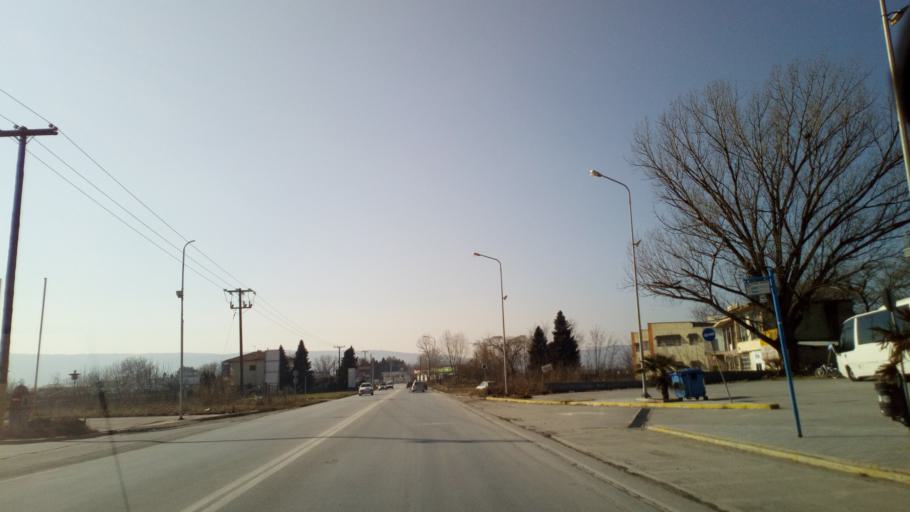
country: GR
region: Central Macedonia
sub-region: Nomos Thessalonikis
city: Lagkadas
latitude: 40.7430
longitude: 23.0543
